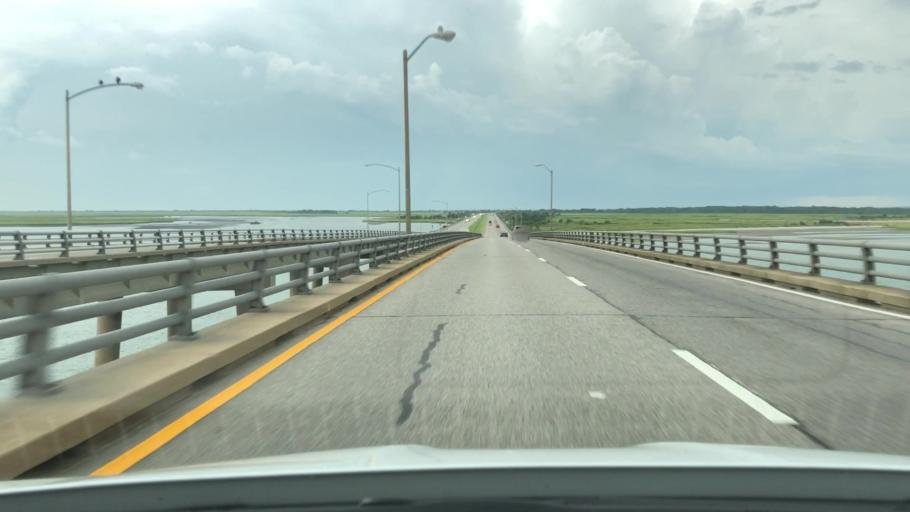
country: US
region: Virginia
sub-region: Northampton County
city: Cape Charles
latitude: 37.1143
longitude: -75.9693
